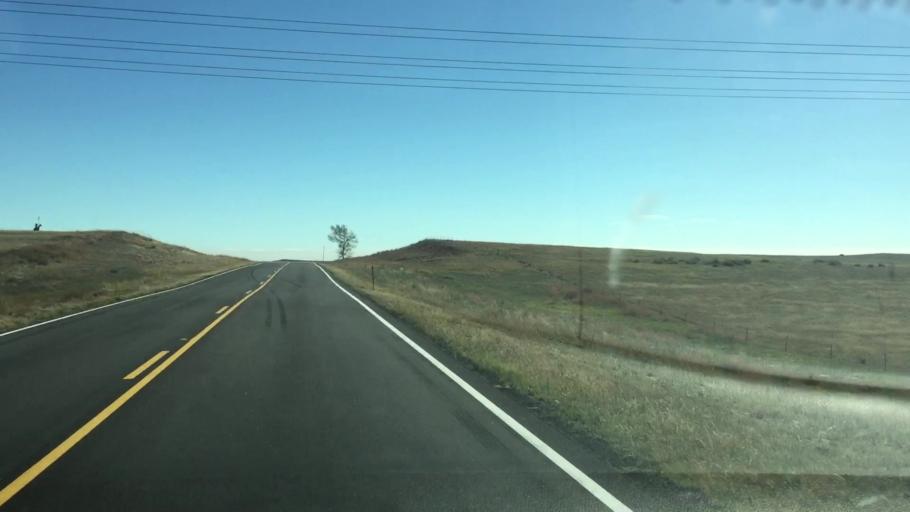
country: US
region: Colorado
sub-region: Lincoln County
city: Limon
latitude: 39.2954
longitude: -103.8719
